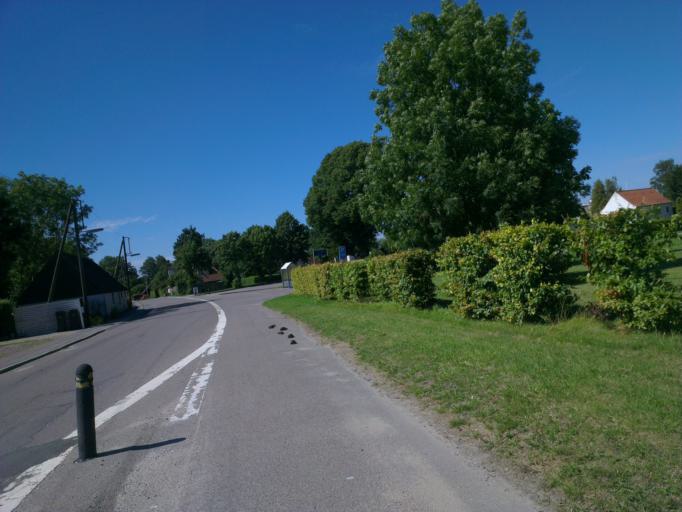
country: DK
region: Capital Region
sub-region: Frederikssund Kommune
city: Frederikssund
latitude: 55.8603
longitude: 12.1004
